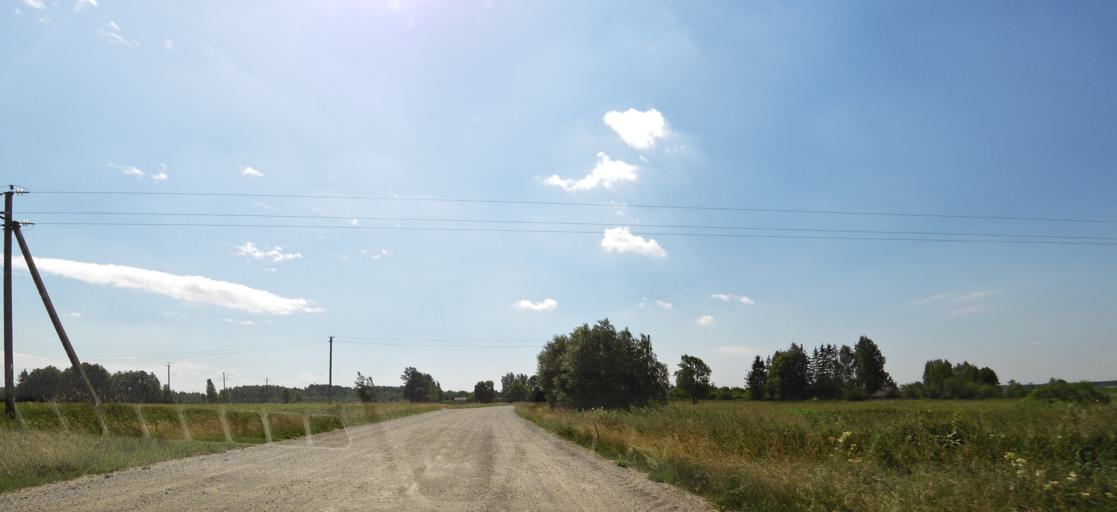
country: LT
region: Panevezys
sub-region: Birzai
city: Birzai
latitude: 56.1909
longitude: 24.9330
